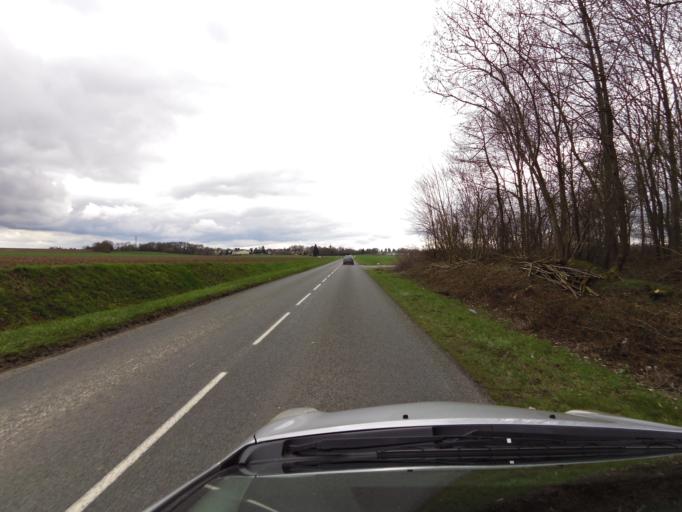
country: FR
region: Picardie
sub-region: Departement de la Somme
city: Chaulnes
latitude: 49.8277
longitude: 2.8114
